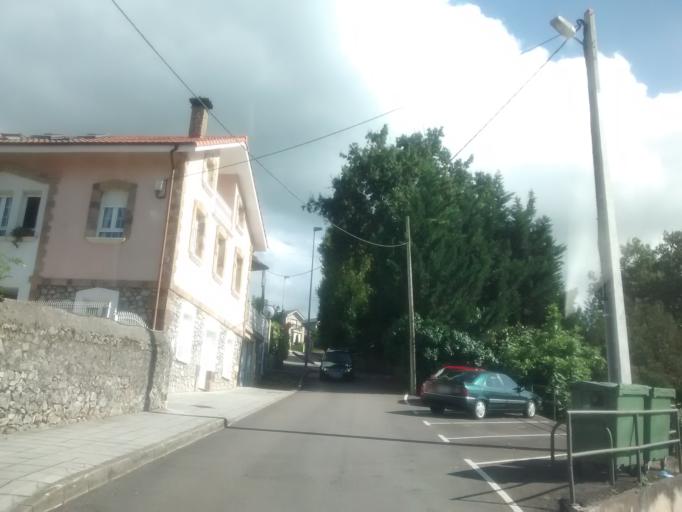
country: ES
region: Cantabria
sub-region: Provincia de Cantabria
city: Lierganes
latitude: 43.3827
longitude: -3.7373
